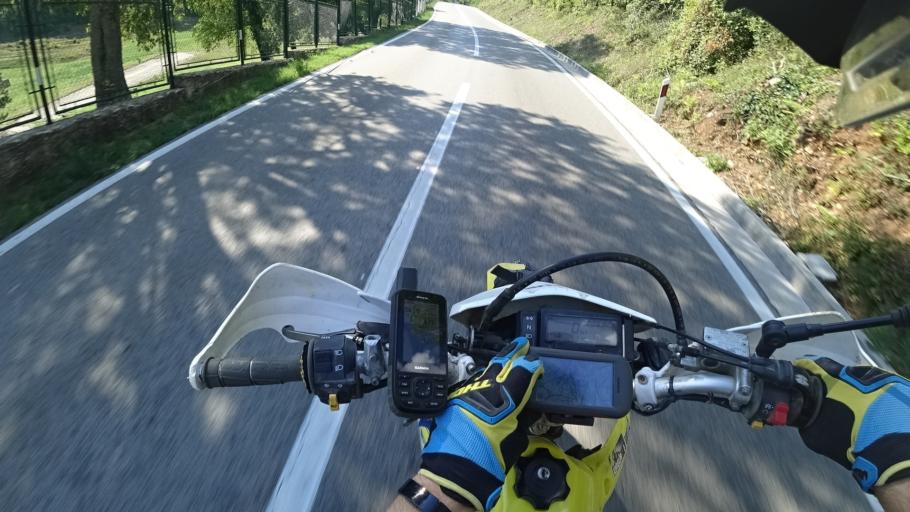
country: HR
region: Sibensko-Kniniska
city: Knin
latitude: 44.0248
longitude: 16.1956
